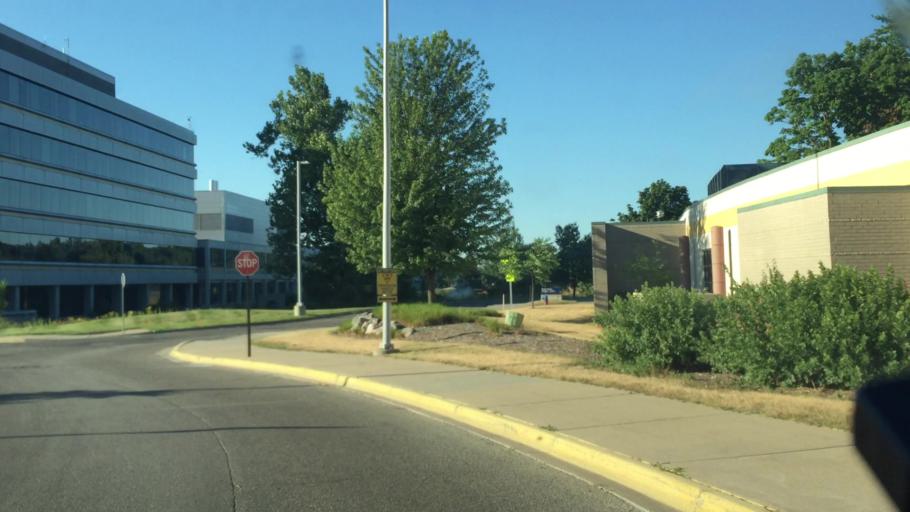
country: US
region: Michigan
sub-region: Washtenaw County
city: Ann Arbor
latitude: 42.3016
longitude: -83.7083
